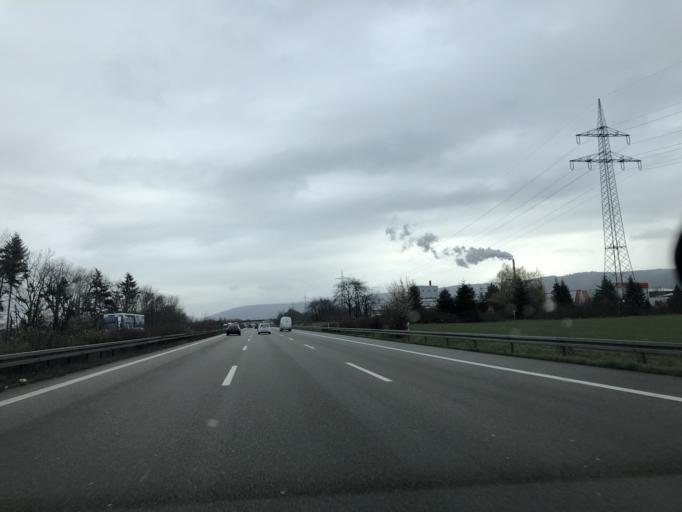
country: DE
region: Baden-Wuerttemberg
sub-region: Karlsruhe Region
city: Malsch
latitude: 48.8934
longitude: 8.3075
